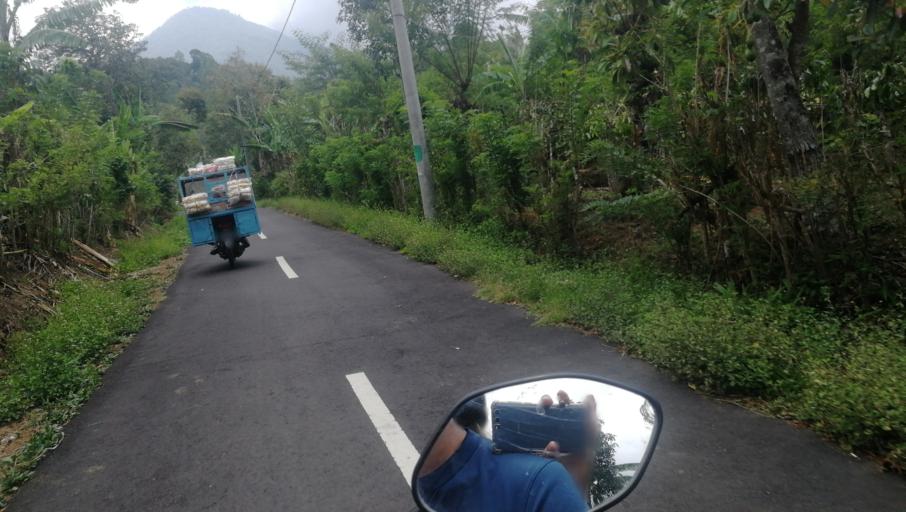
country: ID
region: Bali
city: Munduk
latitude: -8.3035
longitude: 115.0592
